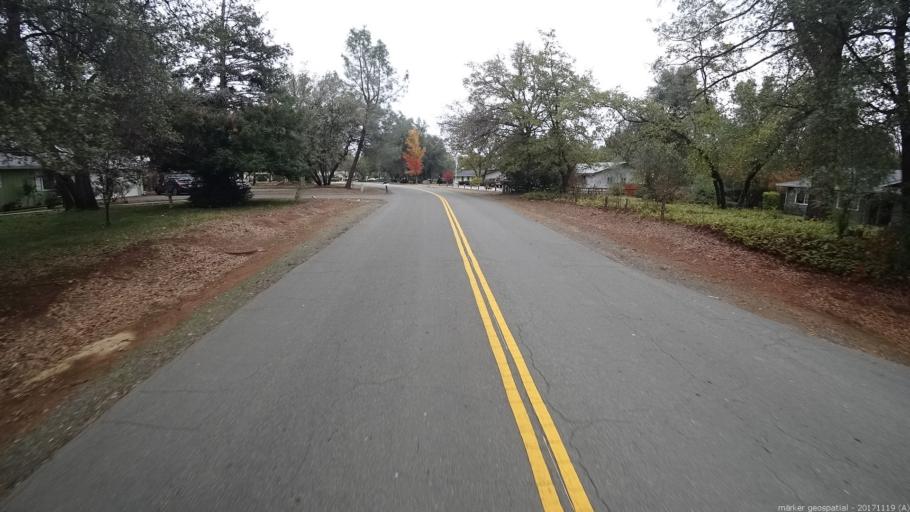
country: US
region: California
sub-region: Shasta County
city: Redding
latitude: 40.4883
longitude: -122.4214
